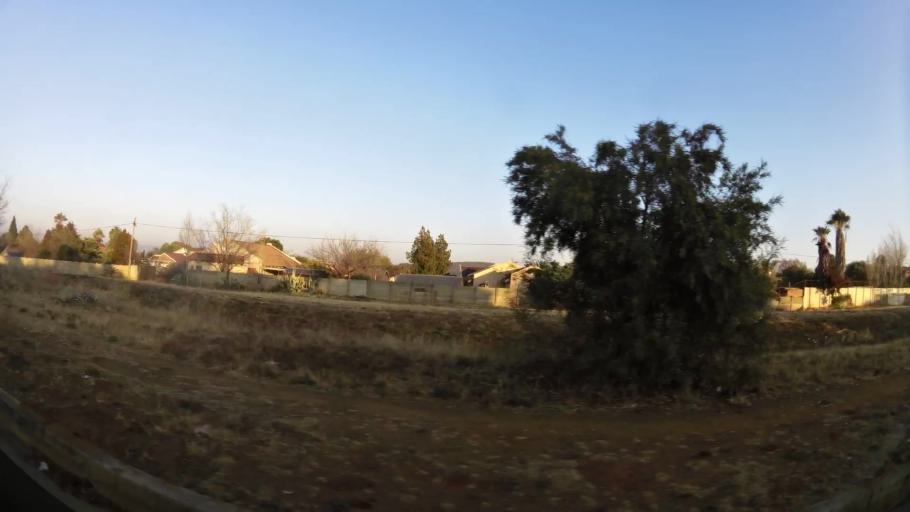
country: ZA
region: Orange Free State
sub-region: Mangaung Metropolitan Municipality
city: Bloemfontein
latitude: -29.0982
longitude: 26.1638
